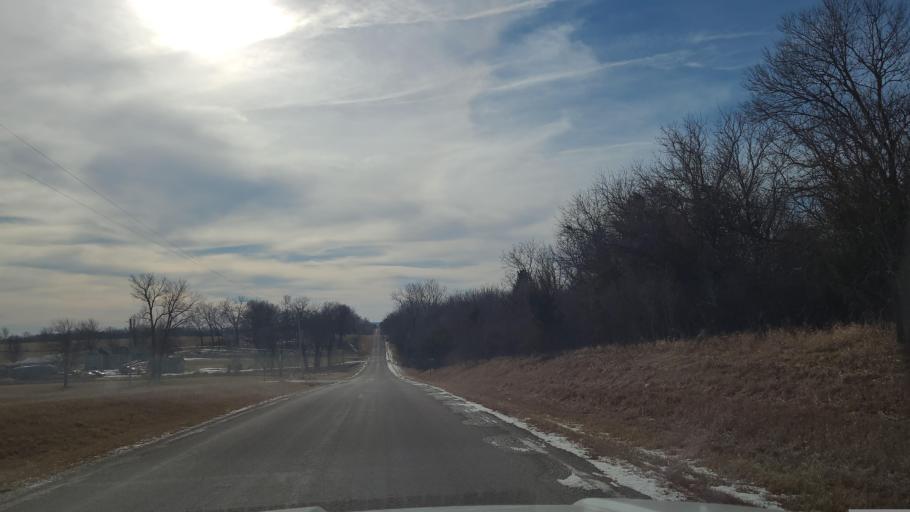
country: US
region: Kansas
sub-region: Douglas County
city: Lawrence
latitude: 38.8944
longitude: -95.1863
